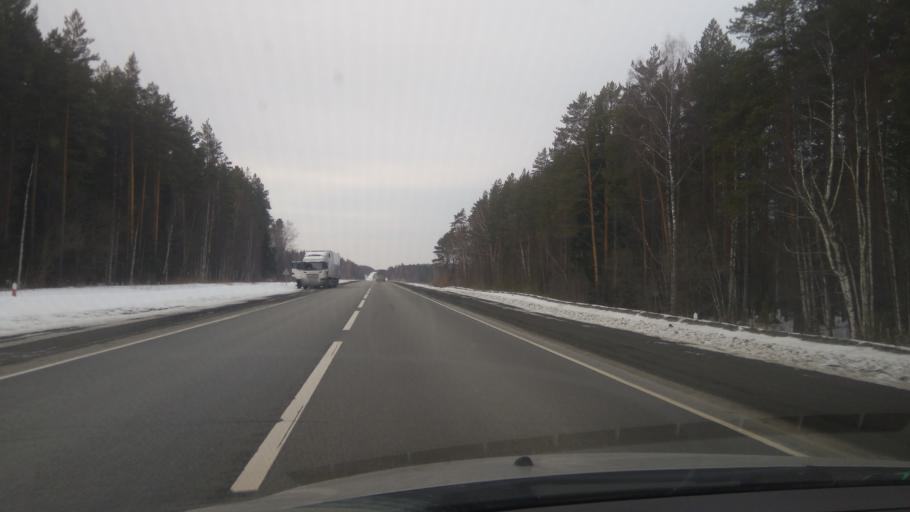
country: RU
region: Sverdlovsk
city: Bisert'
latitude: 56.8279
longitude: 58.7728
